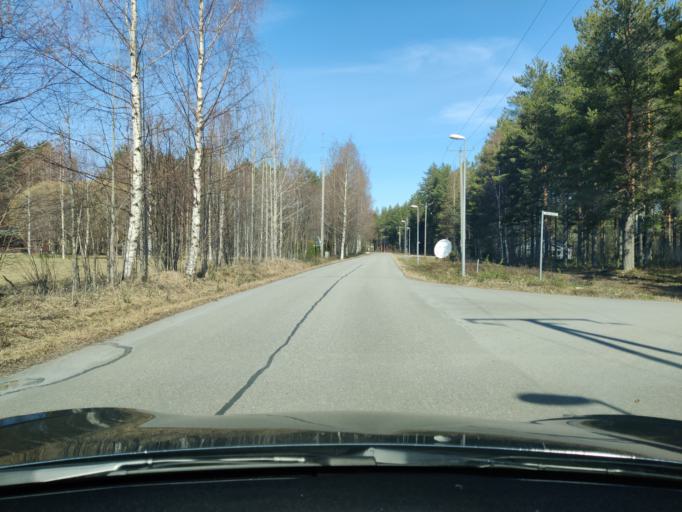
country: FI
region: Northern Savo
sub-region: Kuopio
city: Vehmersalmi
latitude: 62.7702
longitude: 27.9865
